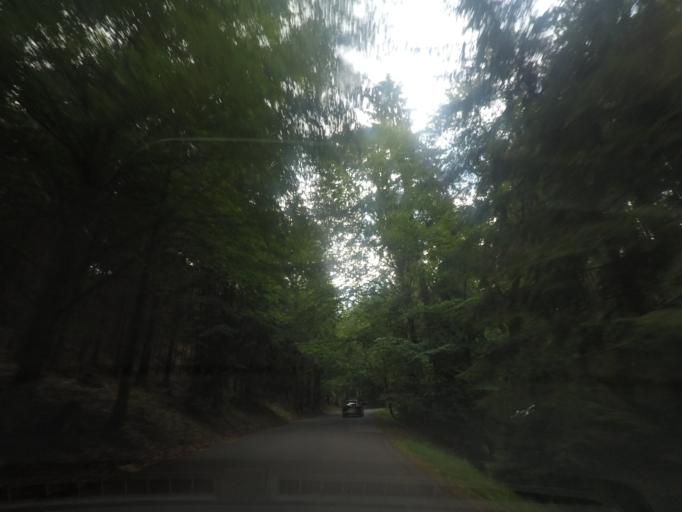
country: CZ
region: Ustecky
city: Mikulasovice
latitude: 50.8671
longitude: 14.3330
